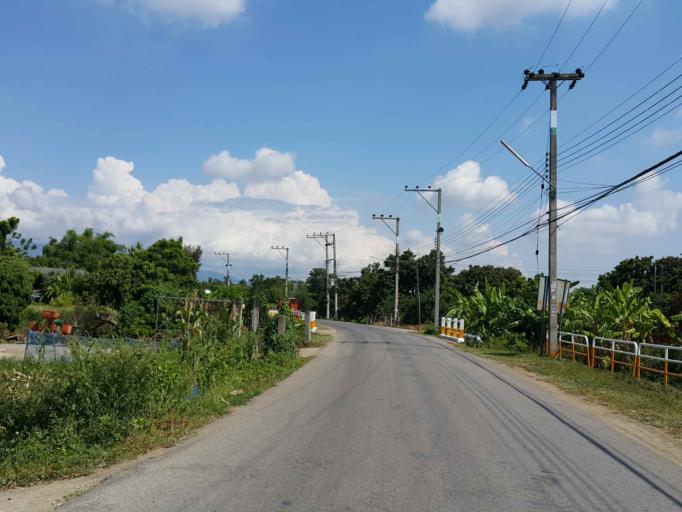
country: TH
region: Chiang Mai
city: Saraphi
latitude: 18.7255
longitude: 99.0478
